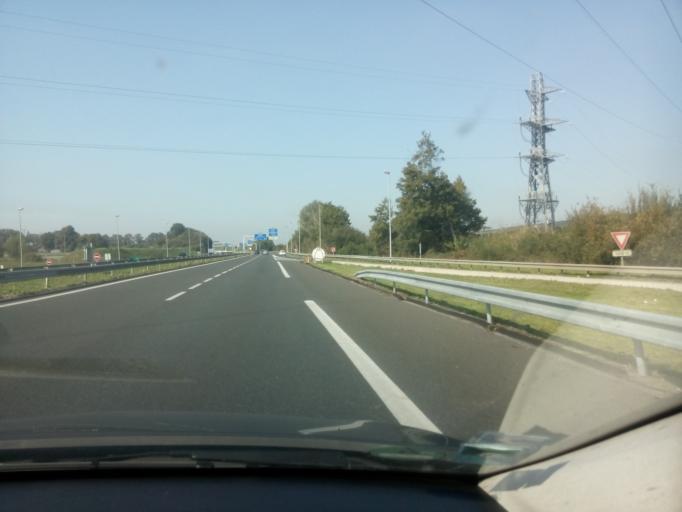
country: FR
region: Pays de la Loire
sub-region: Departement de Maine-et-Loire
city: Ecouflant
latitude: 47.5011
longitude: -0.4908
